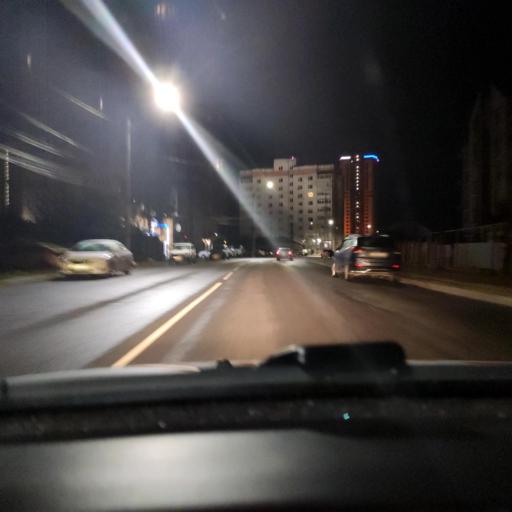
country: RU
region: Voronezj
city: Voronezh
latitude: 51.6519
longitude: 39.1866
